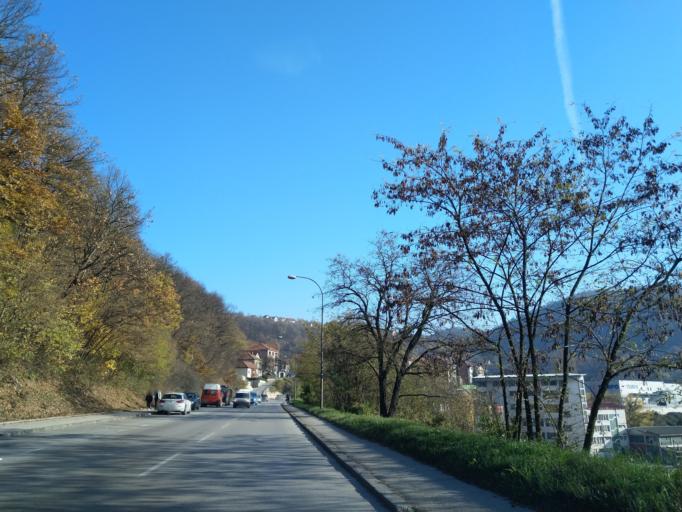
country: RS
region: Central Serbia
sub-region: Zlatiborski Okrug
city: Uzice
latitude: 43.8496
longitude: 19.8616
